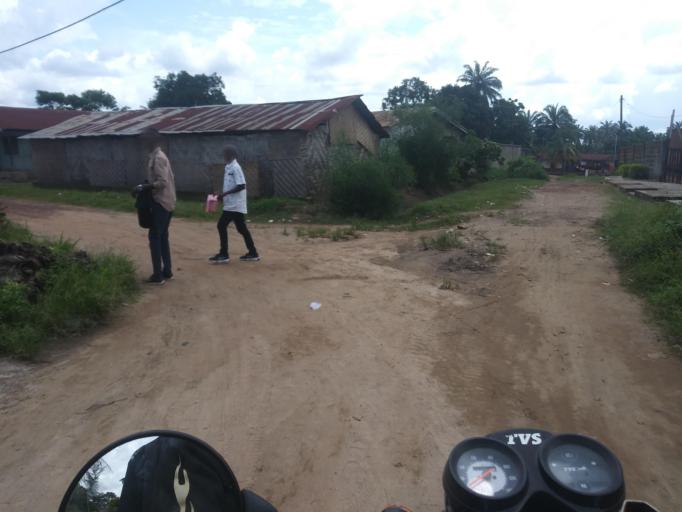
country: SL
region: Northern Province
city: Makeni
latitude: 8.8712
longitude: -12.0427
